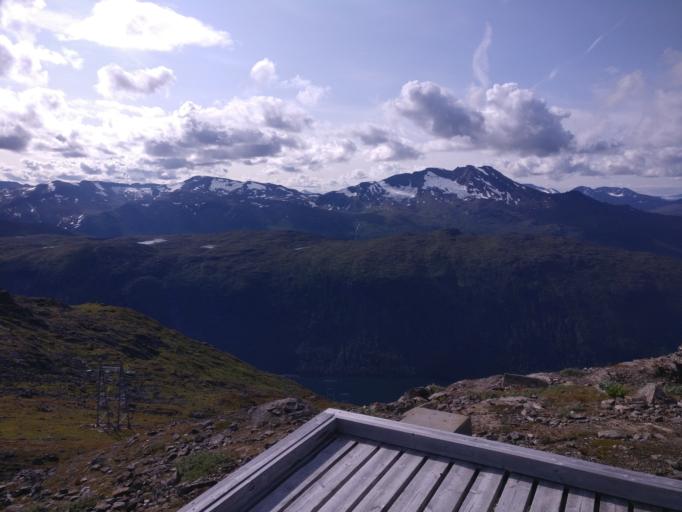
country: NO
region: Nordland
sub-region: Narvik
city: Narvik
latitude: 68.4211
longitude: 17.4818
